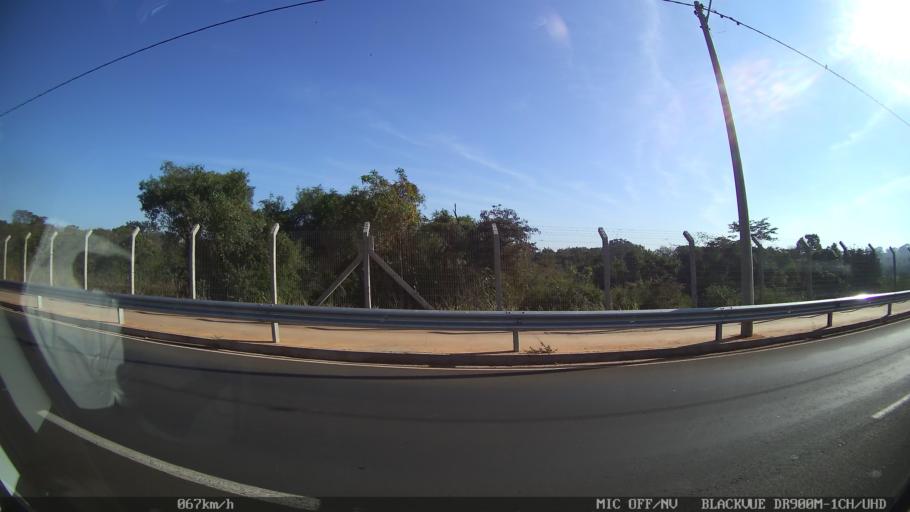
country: BR
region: Sao Paulo
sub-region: Sao Jose Do Rio Preto
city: Sao Jose do Rio Preto
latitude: -20.7618
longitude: -49.3741
